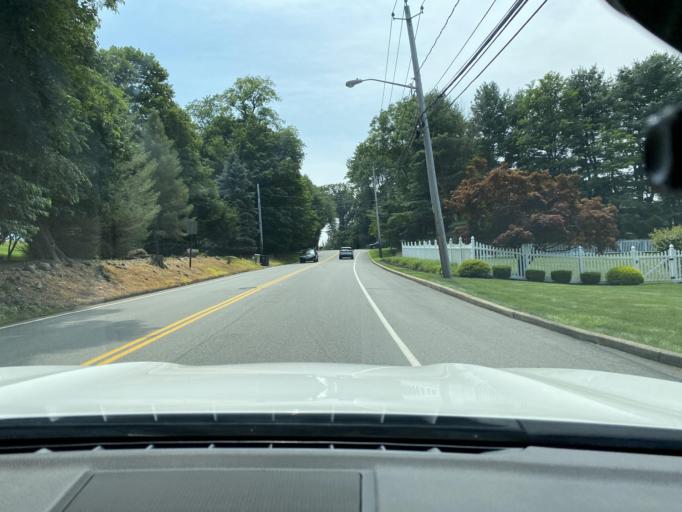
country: US
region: New York
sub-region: Rockland County
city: Airmont
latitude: 41.1055
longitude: -74.1148
